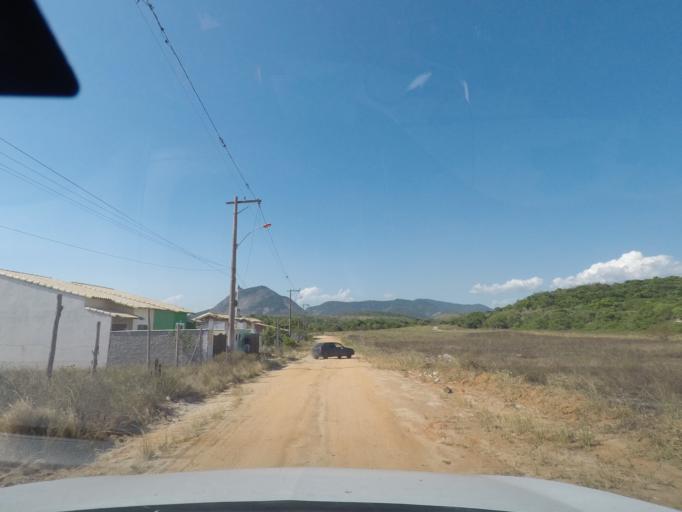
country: BR
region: Rio de Janeiro
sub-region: Marica
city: Marica
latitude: -22.9657
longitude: -42.9038
